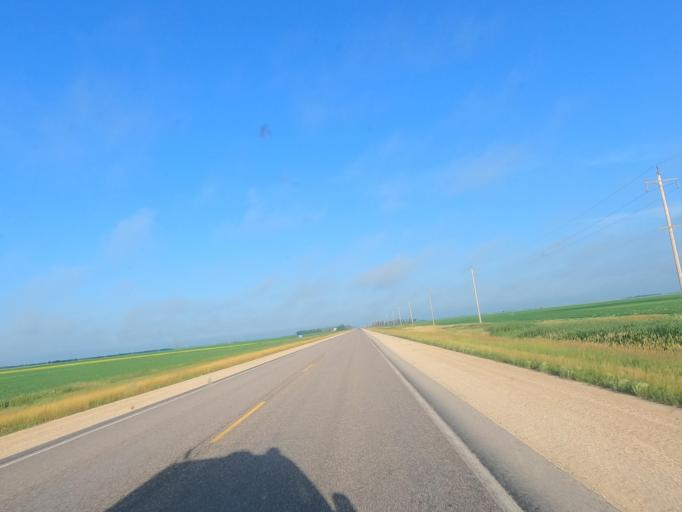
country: CA
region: Manitoba
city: Headingley
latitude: 49.7686
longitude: -97.4432
